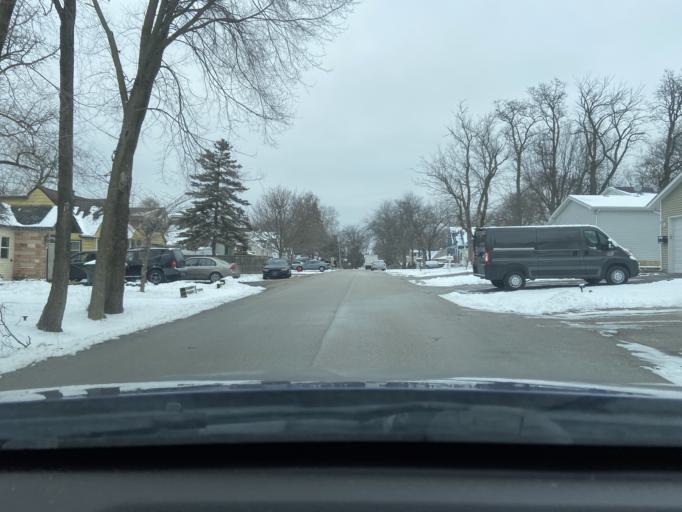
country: US
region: Illinois
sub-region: Lake County
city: Round Lake Park
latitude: 42.3557
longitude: -88.0807
